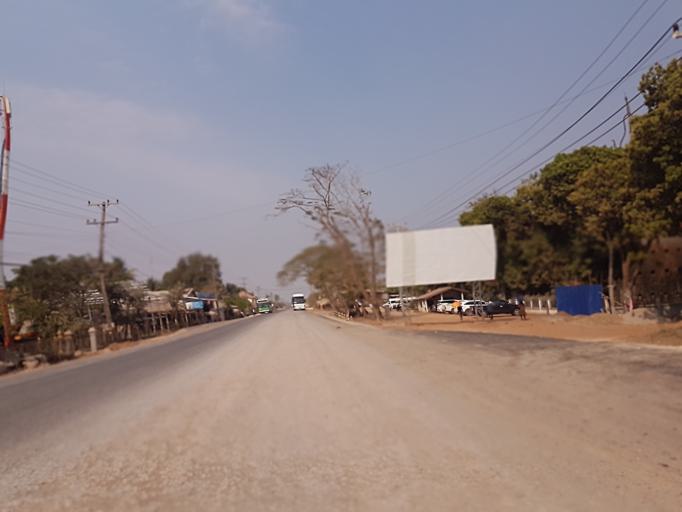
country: TH
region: Nong Khai
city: Nong Khai
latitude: 17.9121
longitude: 102.7639
